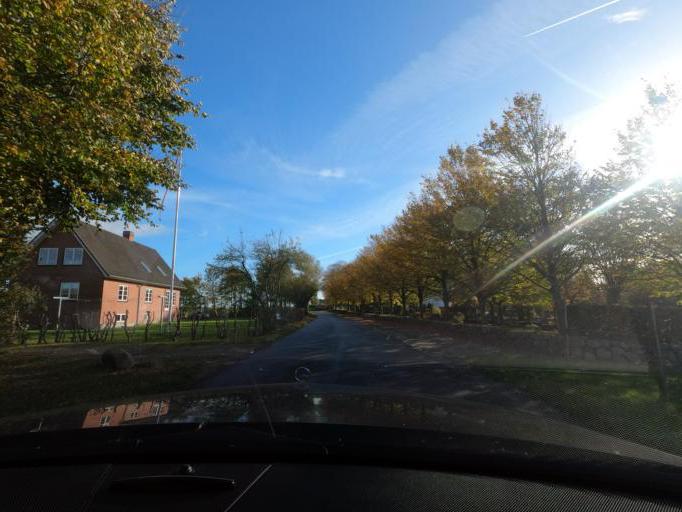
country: DK
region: South Denmark
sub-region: Sonderborg Kommune
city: Dybbol
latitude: 54.9203
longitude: 9.7222
